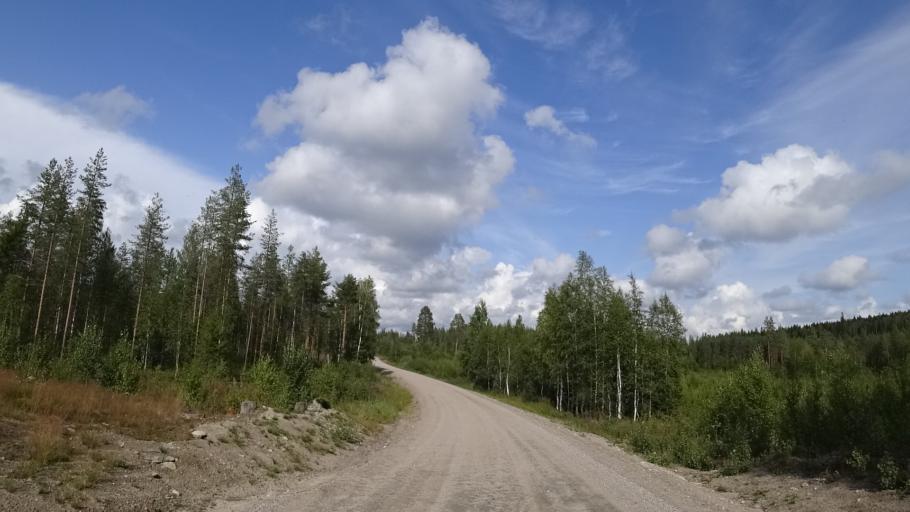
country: FI
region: North Karelia
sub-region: Pielisen Karjala
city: Lieksa
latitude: 63.5764
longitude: 30.1236
